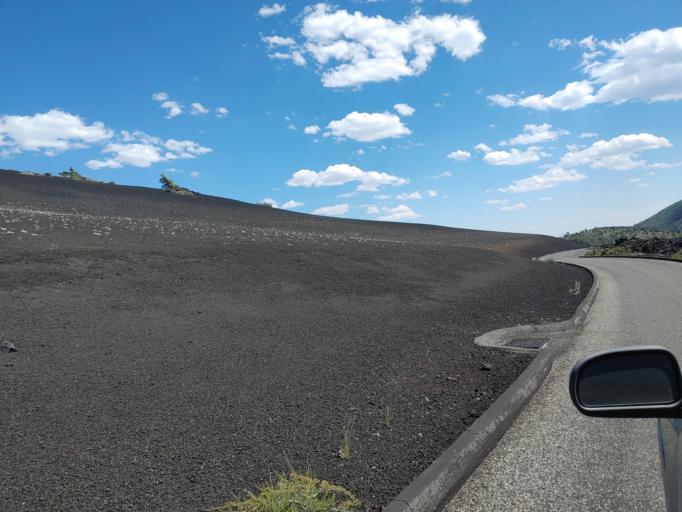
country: US
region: Idaho
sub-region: Butte County
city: Arco
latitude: 43.4420
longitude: -113.5542
